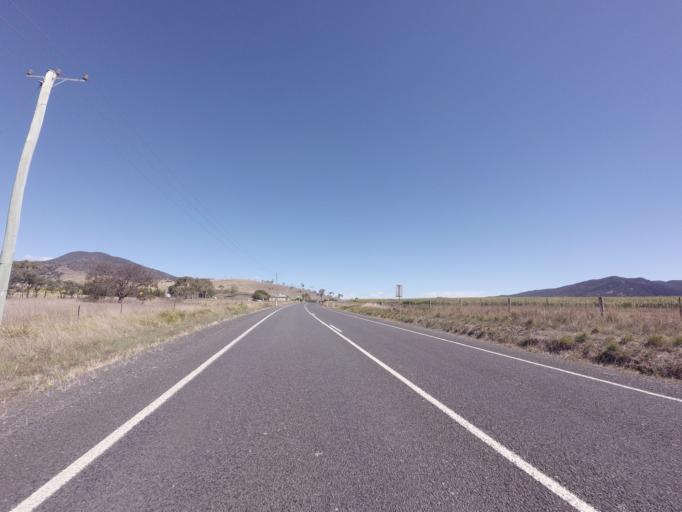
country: AU
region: Tasmania
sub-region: Break O'Day
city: St Helens
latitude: -41.7172
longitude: 147.8346
